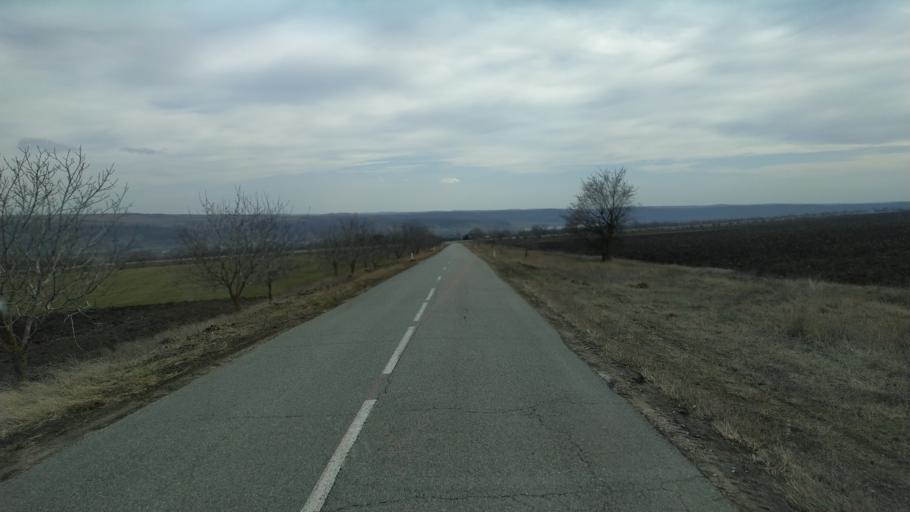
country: MD
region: Nisporeni
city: Nisporeni
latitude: 46.9406
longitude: 28.2450
